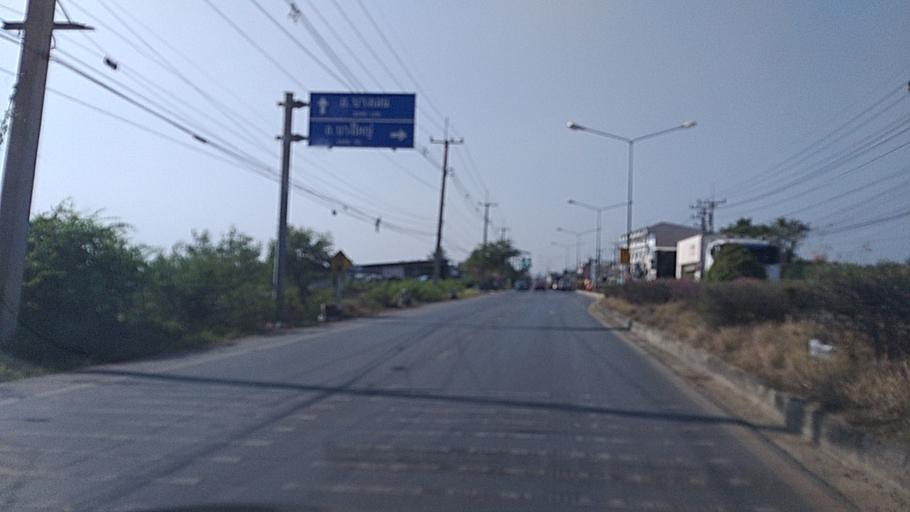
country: TH
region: Nonthaburi
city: Bang Yai
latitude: 13.8735
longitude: 100.2925
